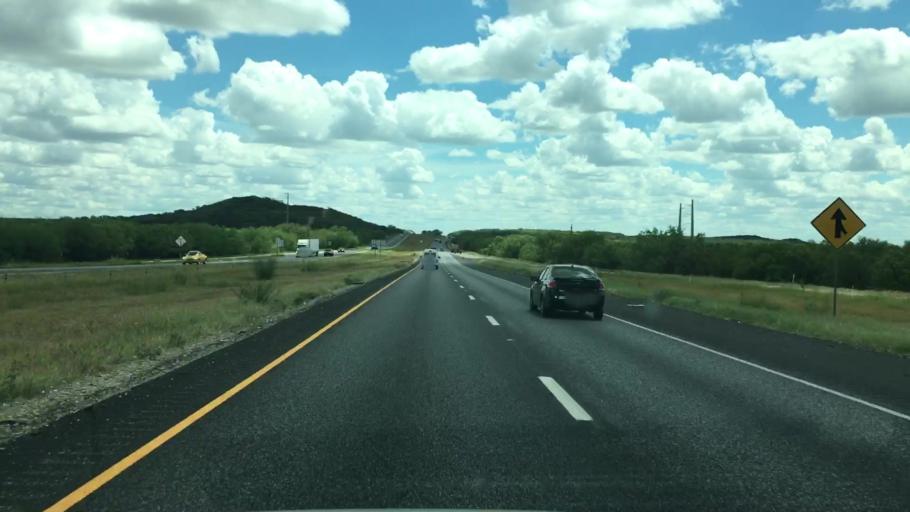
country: US
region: Texas
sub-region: Live Oak County
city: Three Rivers
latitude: 28.7300
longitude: -98.2881
